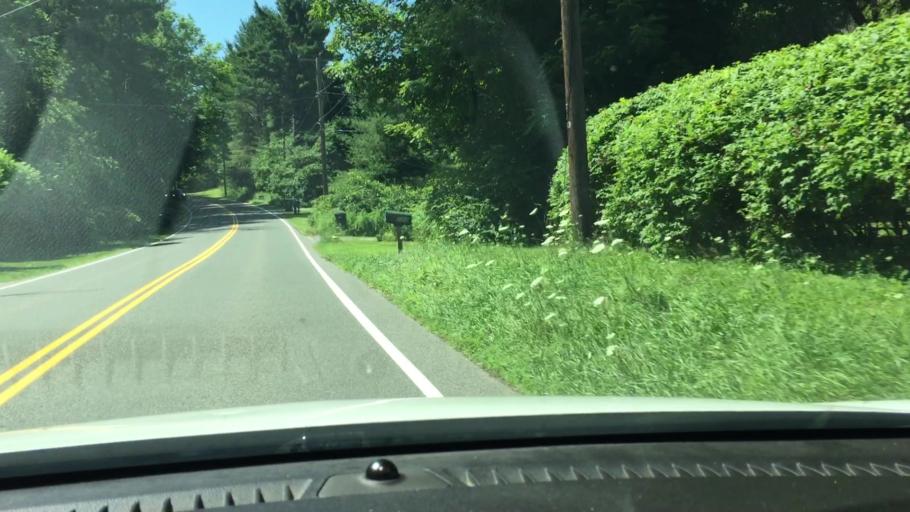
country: US
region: Massachusetts
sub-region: Berkshire County
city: Lenox
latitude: 42.3865
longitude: -73.2565
